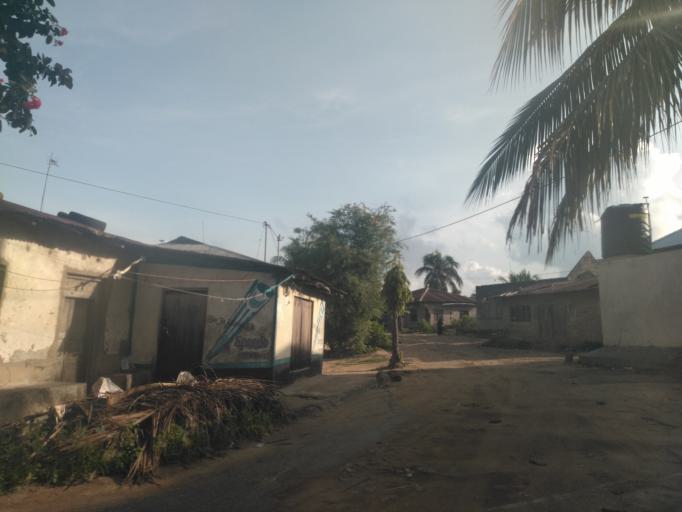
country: TZ
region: Zanzibar Urban/West
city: Zanzibar
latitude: -6.1765
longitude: 39.2129
